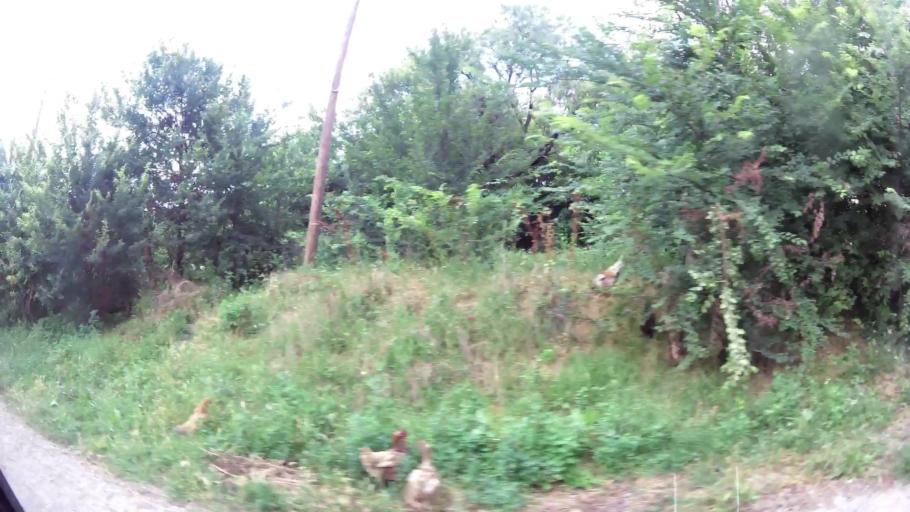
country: GR
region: West Macedonia
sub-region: Nomos Kozanis
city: Koila
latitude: 40.3486
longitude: 21.8294
